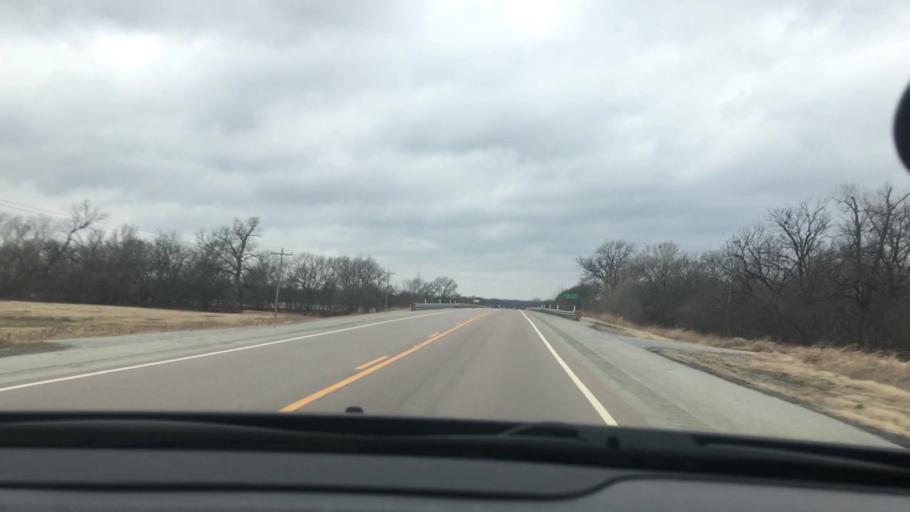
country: US
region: Oklahoma
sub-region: Atoka County
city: Atoka
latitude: 34.3724
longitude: -96.3111
